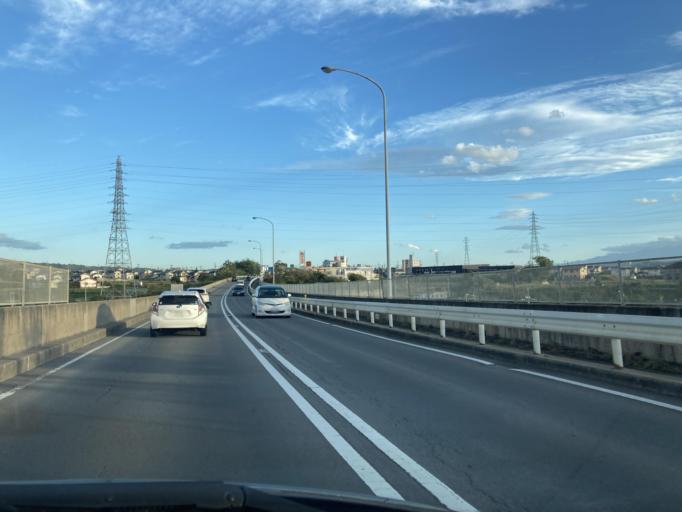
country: JP
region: Nagano
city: Ueda
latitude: 36.4086
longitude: 138.2680
